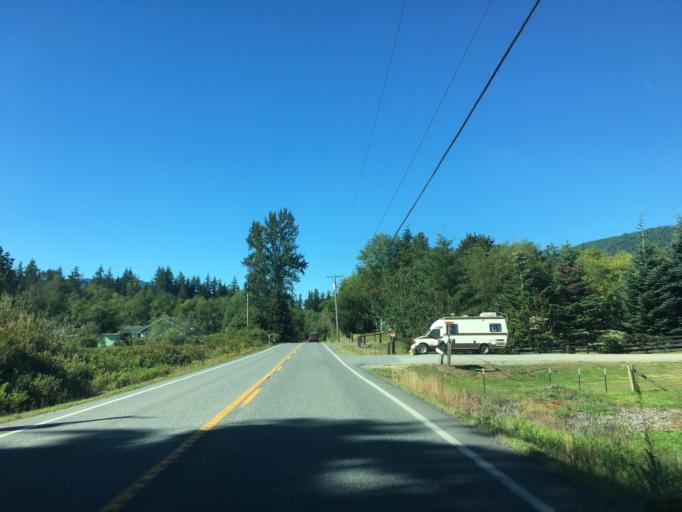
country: US
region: Washington
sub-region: Skagit County
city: Sedro-Woolley
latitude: 48.5531
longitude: -122.2250
